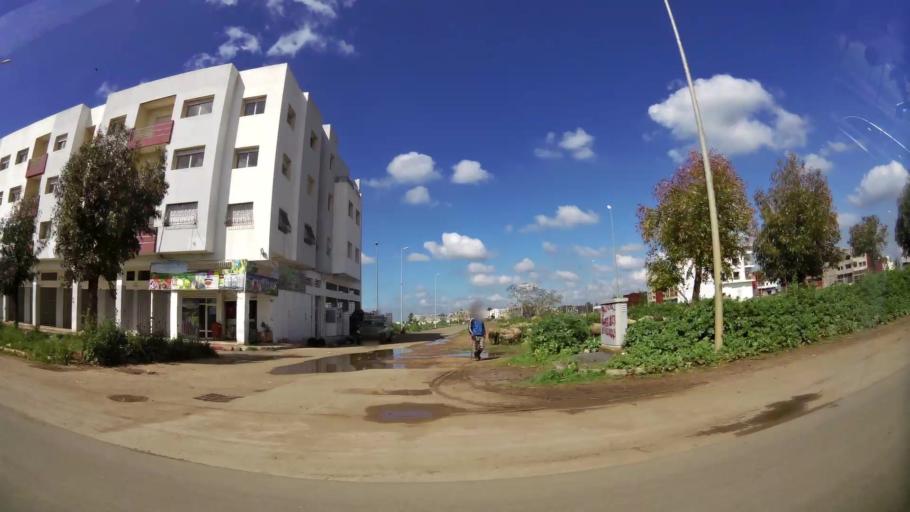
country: MA
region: Grand Casablanca
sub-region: Mediouna
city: Mediouna
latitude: 33.4479
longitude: -7.5049
